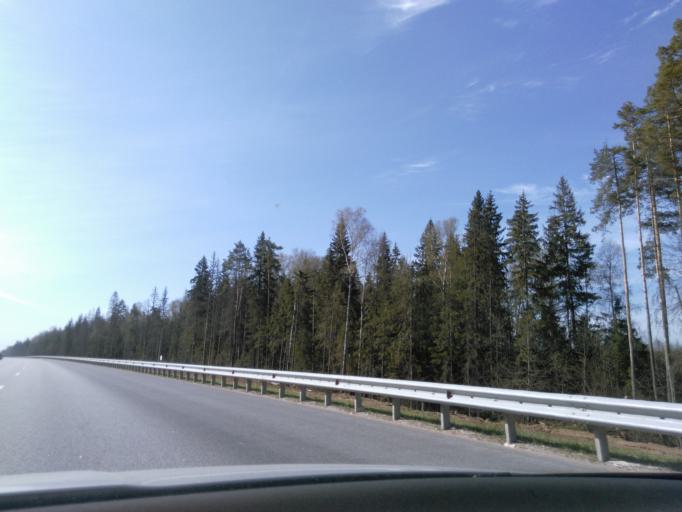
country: RU
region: Moskovskaya
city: Rzhavki
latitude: 56.0266
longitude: 37.2727
